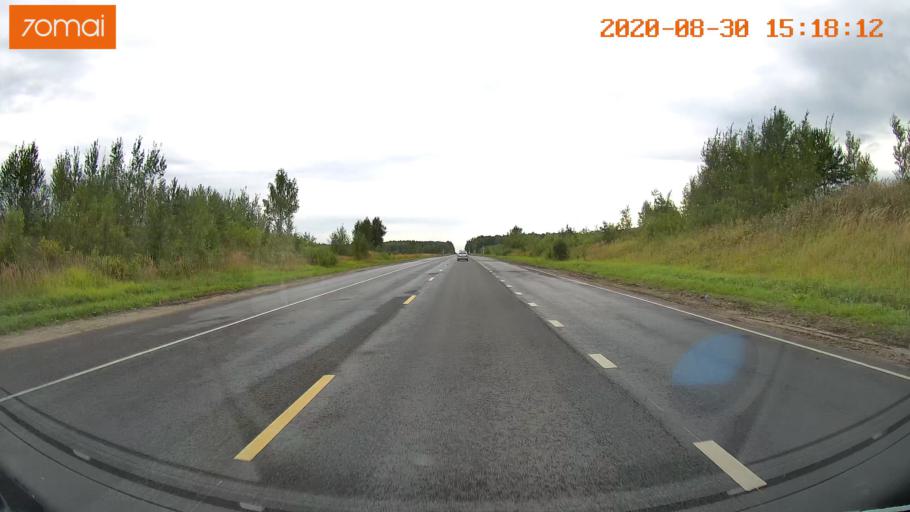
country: RU
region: Ivanovo
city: Rodniki
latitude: 57.1257
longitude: 41.7960
